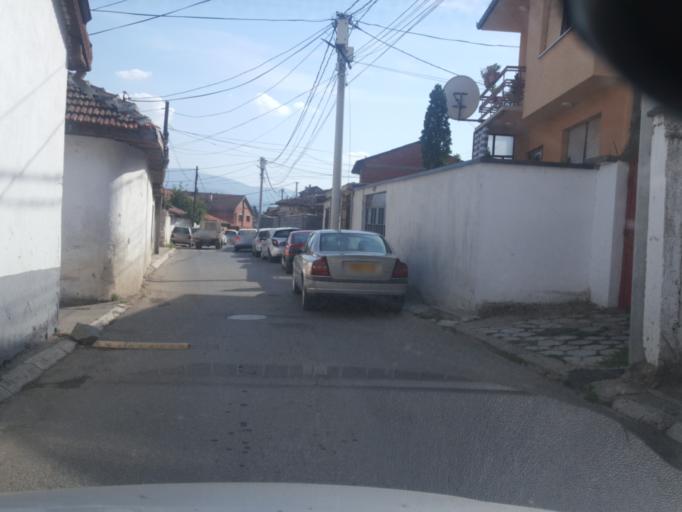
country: XK
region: Gjakova
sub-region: Komuna e Gjakoves
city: Gjakove
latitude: 42.3802
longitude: 20.4244
